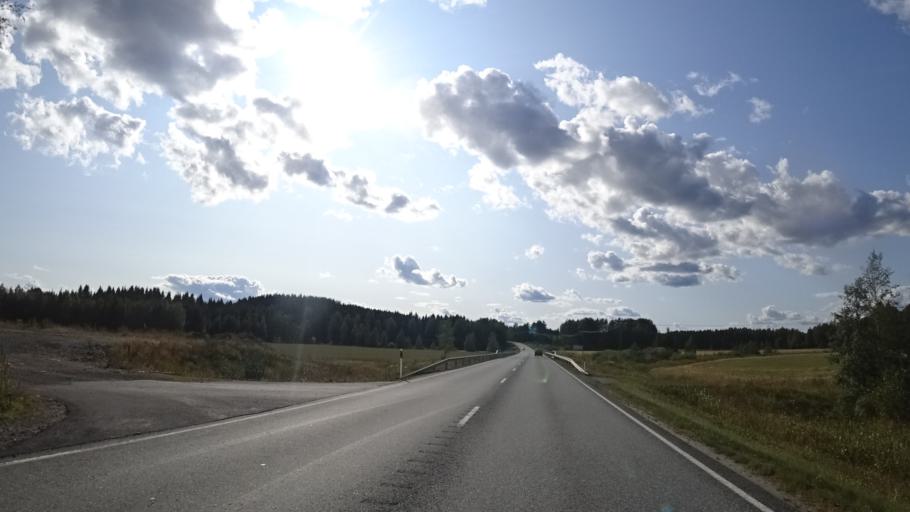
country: FI
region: North Karelia
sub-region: Keski-Karjala
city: Kitee
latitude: 62.0902
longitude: 30.0228
